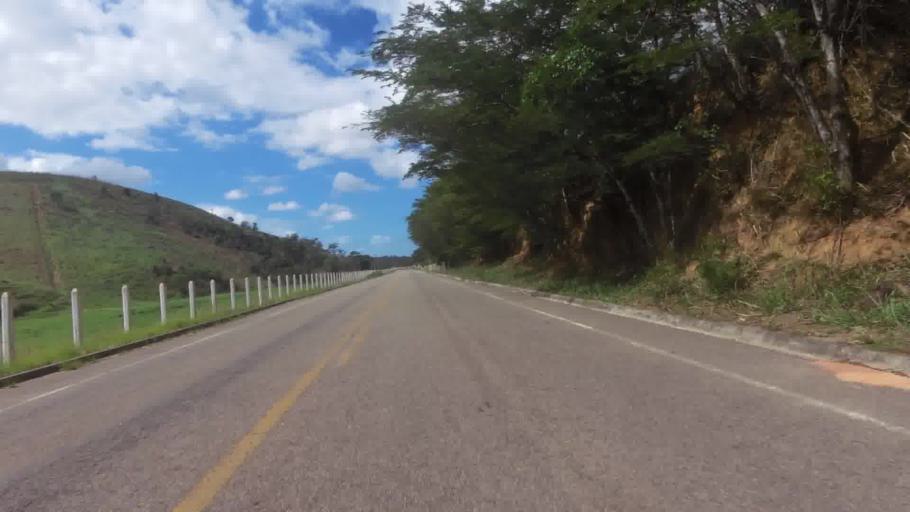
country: BR
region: Espirito Santo
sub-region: Marataizes
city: Marataizes
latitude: -21.1322
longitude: -41.0068
